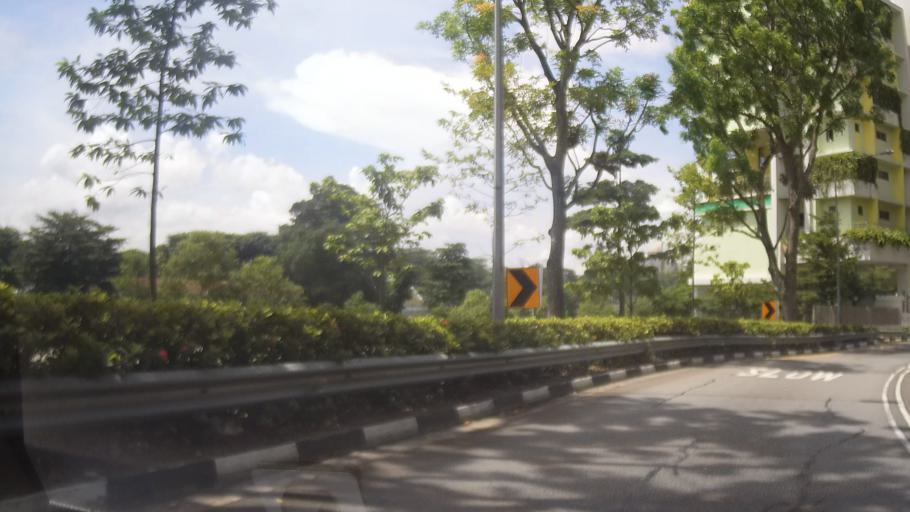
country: MY
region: Johor
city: Johor Bahru
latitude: 1.3963
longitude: 103.7515
